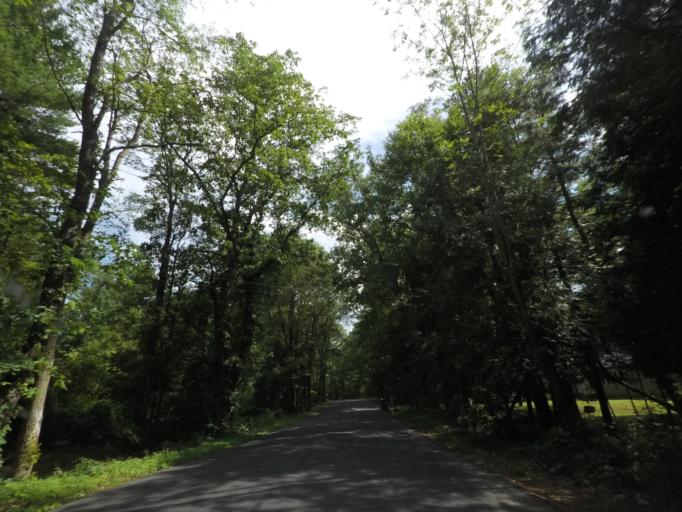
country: US
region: New York
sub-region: Rensselaer County
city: Averill Park
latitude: 42.6531
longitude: -73.5502
